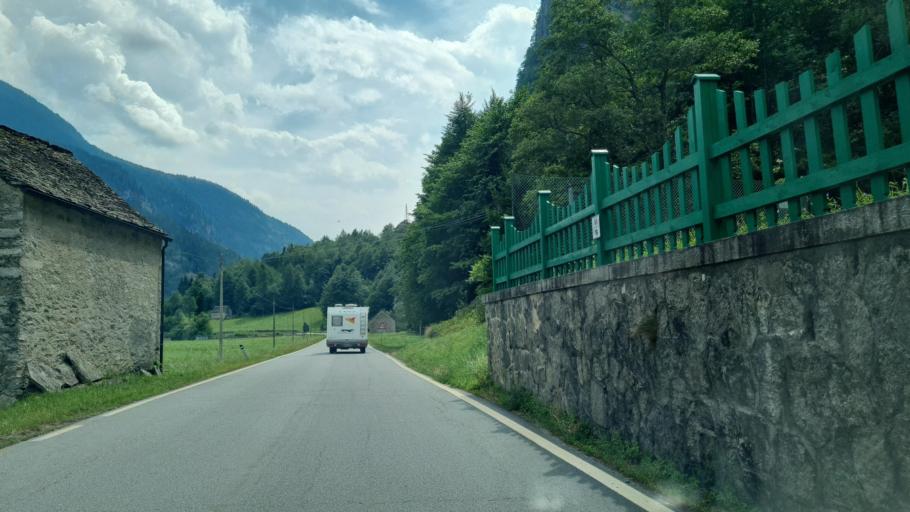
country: IT
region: Piedmont
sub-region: Provincia Verbano-Cusio-Ossola
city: Premia
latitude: 46.2887
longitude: 8.3553
